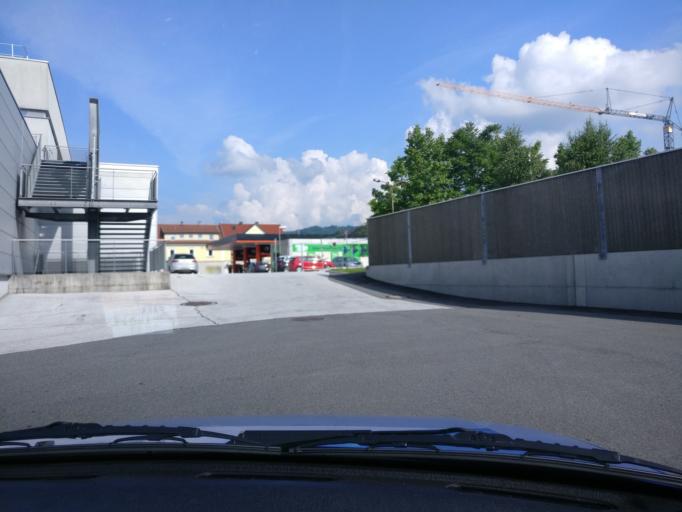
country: AT
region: Carinthia
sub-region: Klagenfurt am Woerthersee
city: Klagenfurt am Woerthersee
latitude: 46.6094
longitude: 14.2984
